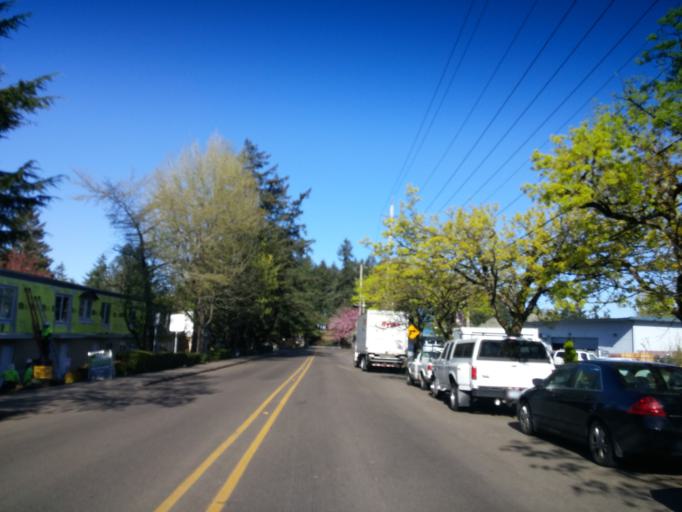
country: US
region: Oregon
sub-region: Washington County
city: Cedar Hills
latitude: 45.5099
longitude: -122.7850
